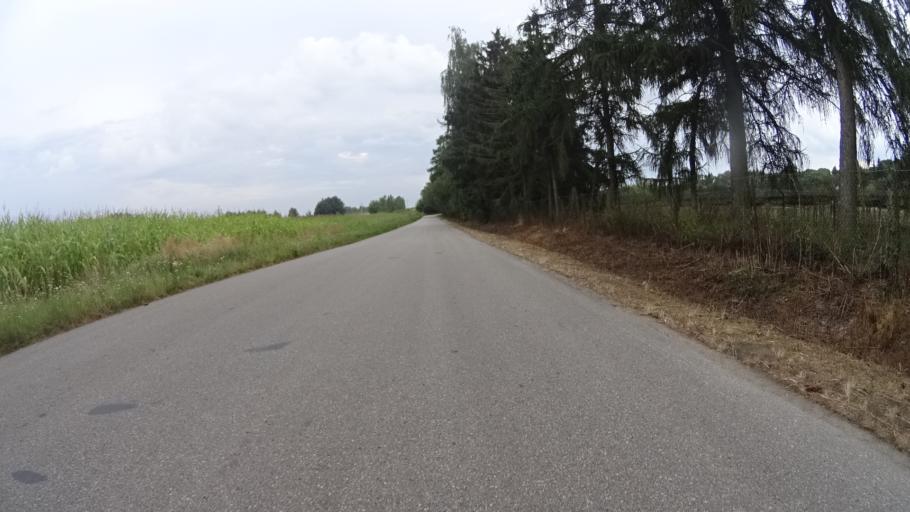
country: PL
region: Masovian Voivodeship
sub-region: Powiat grojecki
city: Goszczyn
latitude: 51.6870
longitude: 20.8608
